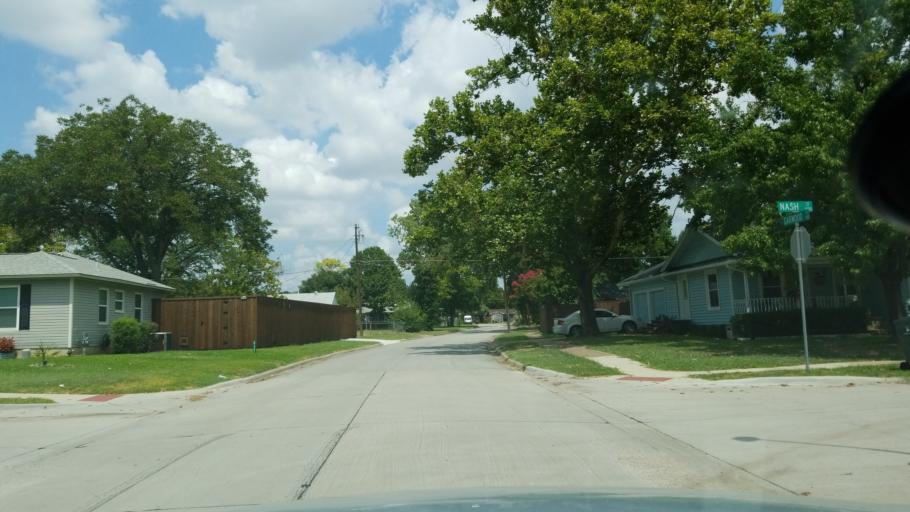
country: US
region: Texas
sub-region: Dallas County
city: Garland
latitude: 32.9207
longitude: -96.6520
